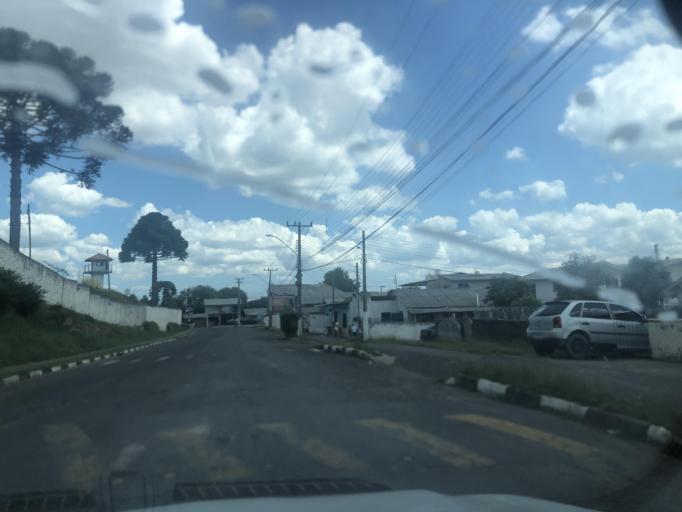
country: BR
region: Santa Catarina
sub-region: Lages
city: Lages
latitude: -27.7951
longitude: -50.3137
